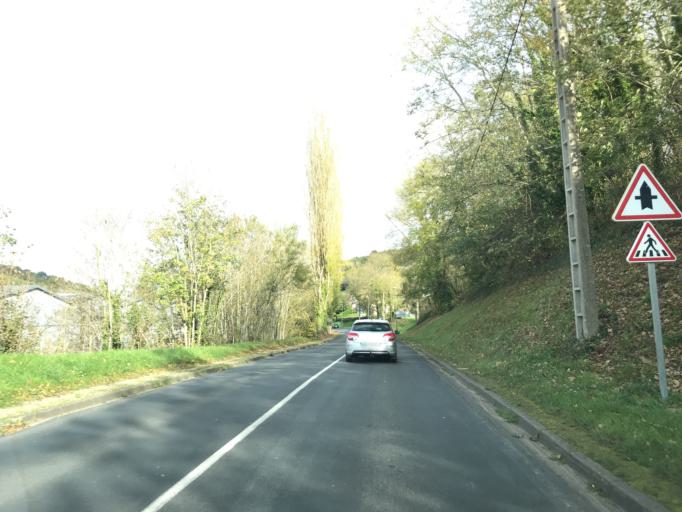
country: FR
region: Haute-Normandie
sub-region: Departement de l'Eure
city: Les Andelys
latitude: 49.2541
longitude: 1.4160
